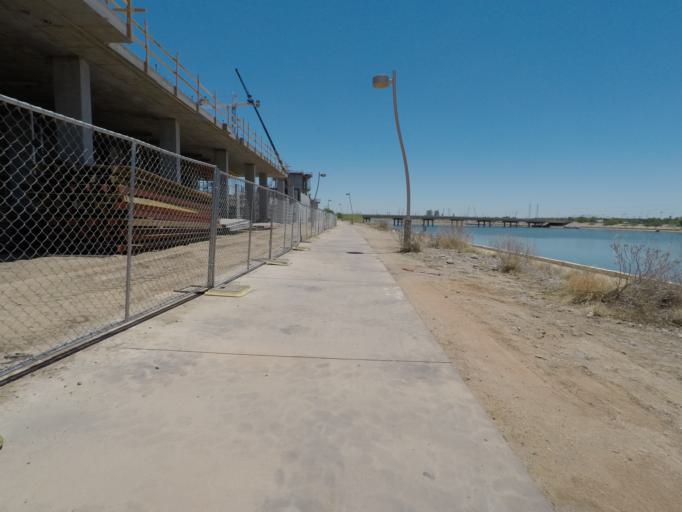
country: US
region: Arizona
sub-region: Maricopa County
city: Tempe Junction
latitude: 33.4332
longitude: -111.9301
